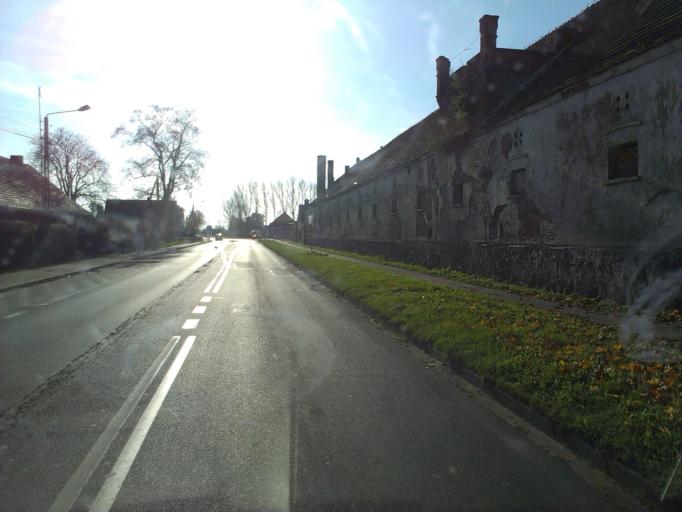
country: PL
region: West Pomeranian Voivodeship
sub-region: Powiat pyrzycki
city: Pyrzyce
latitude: 53.1854
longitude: 14.8401
